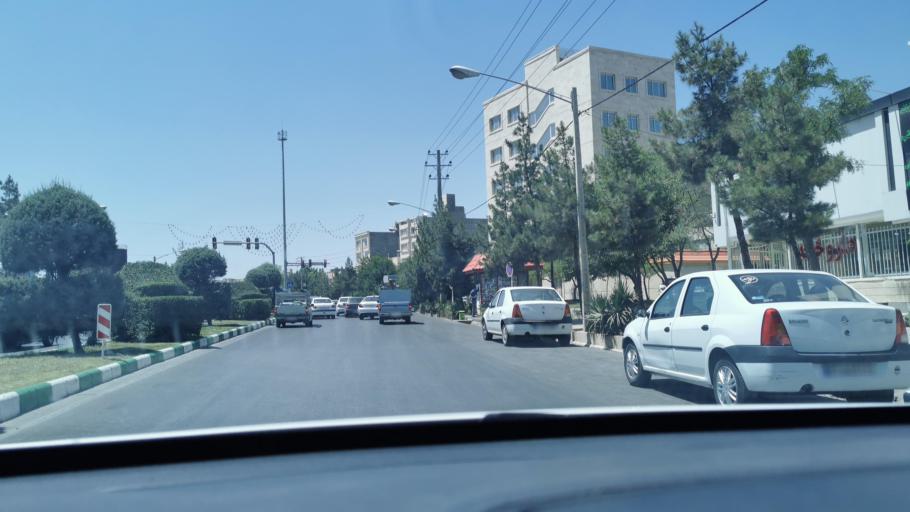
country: IR
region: Razavi Khorasan
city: Mashhad
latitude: 36.3399
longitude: 59.4842
